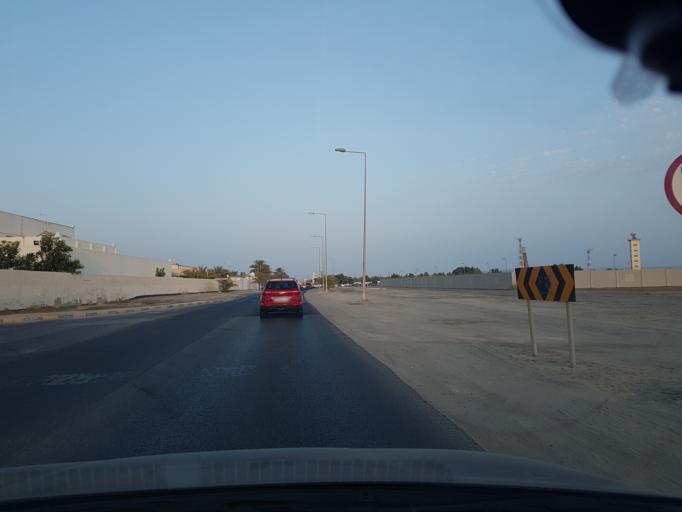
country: BH
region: Muharraq
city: Al Muharraq
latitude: 26.2764
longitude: 50.6374
